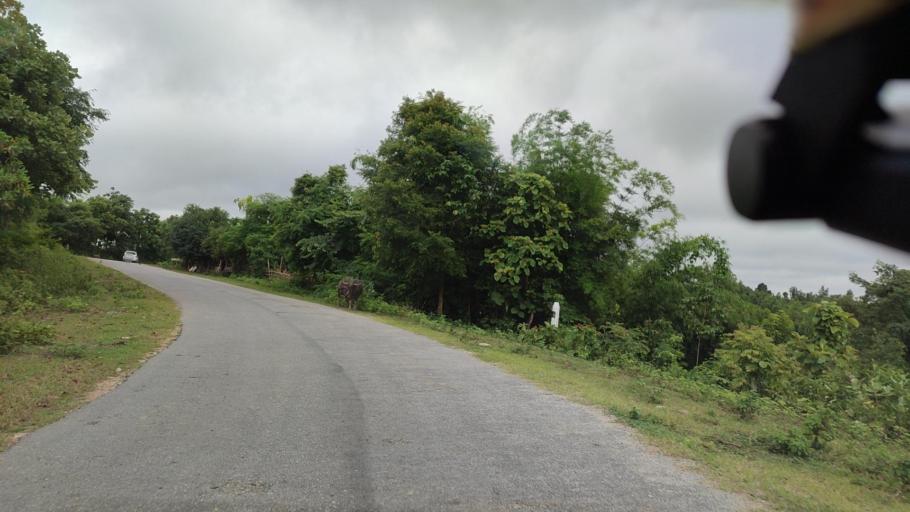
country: MM
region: Magway
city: Taungdwingyi
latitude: 19.9979
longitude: 95.8759
